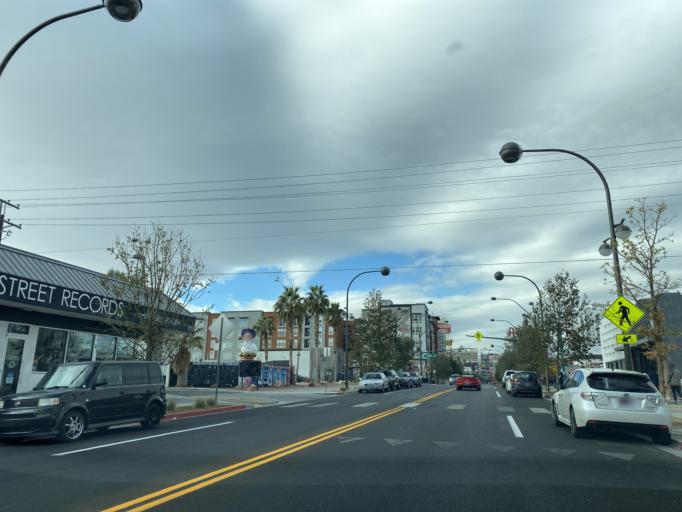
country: US
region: Nevada
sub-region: Clark County
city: Las Vegas
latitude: 36.1665
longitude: -115.1341
